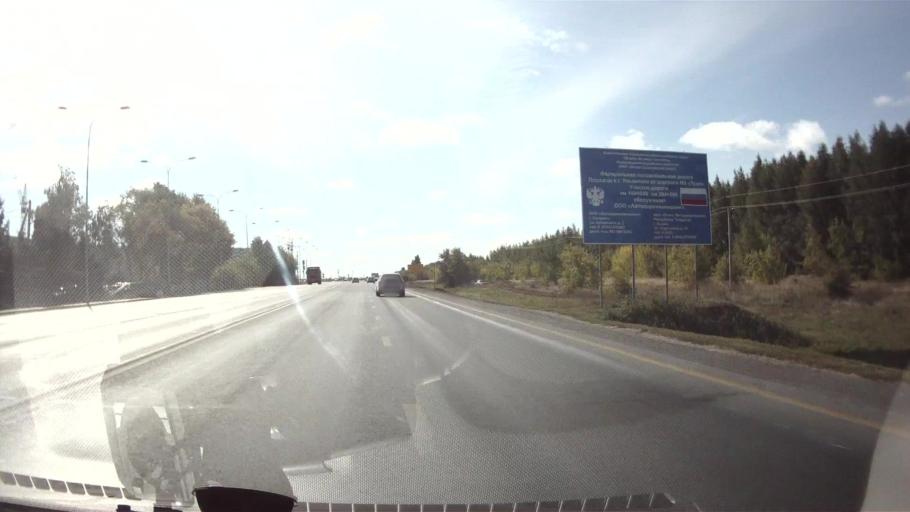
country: RU
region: Ulyanovsk
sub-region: Ulyanovskiy Rayon
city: Ulyanovsk
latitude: 54.2885
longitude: 48.2556
